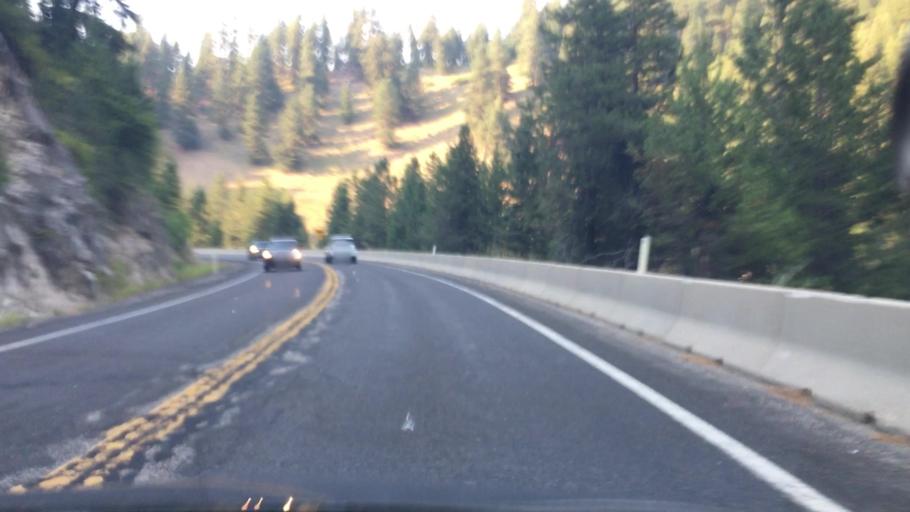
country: US
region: Idaho
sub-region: Valley County
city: Cascade
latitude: 44.2634
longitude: -116.0671
